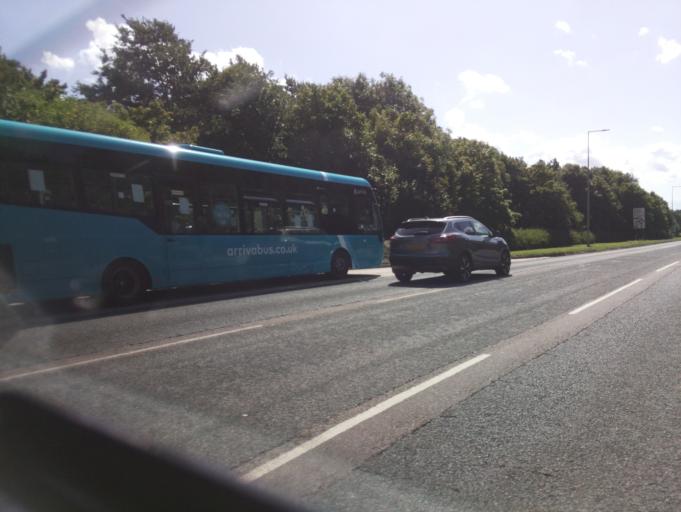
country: GB
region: England
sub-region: Milton Keynes
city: Shenley Church End
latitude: 52.0141
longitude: -0.7801
